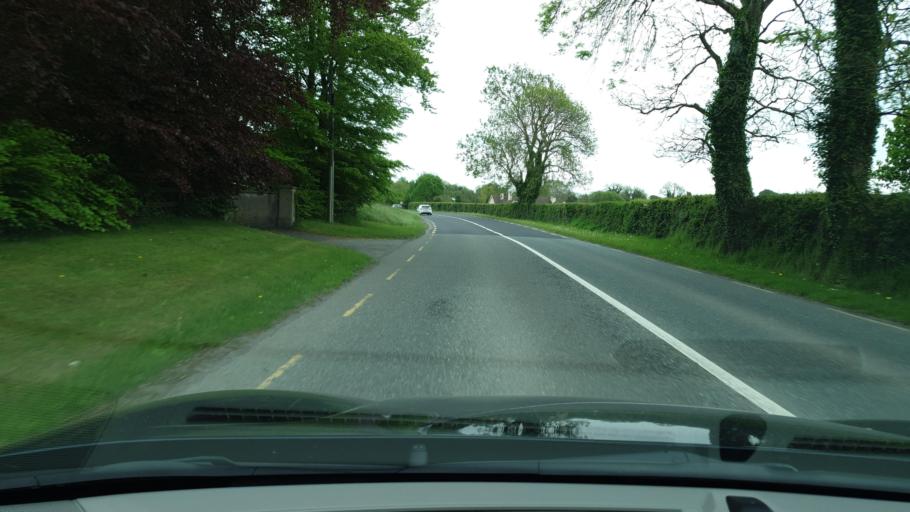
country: IE
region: Leinster
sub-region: An Mhi
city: Dunboyne
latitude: 53.4523
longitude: -6.4888
